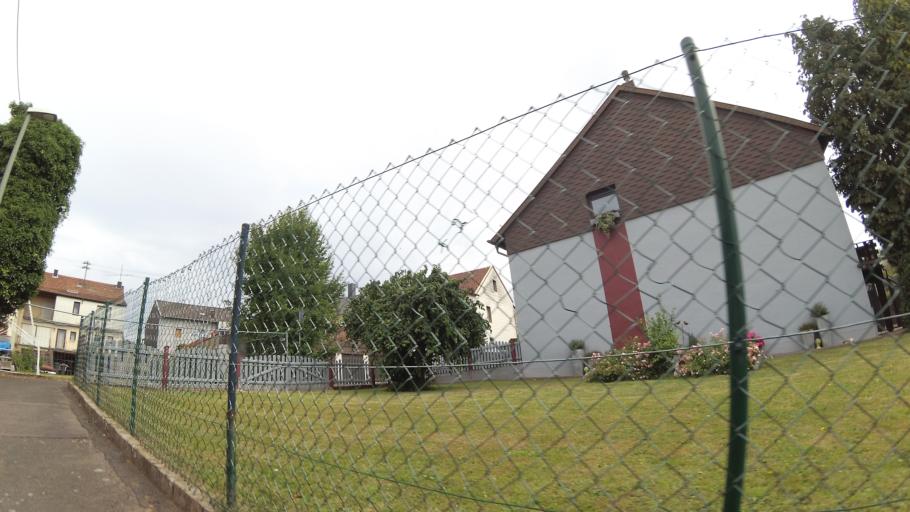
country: DE
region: Saarland
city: Schwalbach
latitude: 49.3181
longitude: 6.8115
